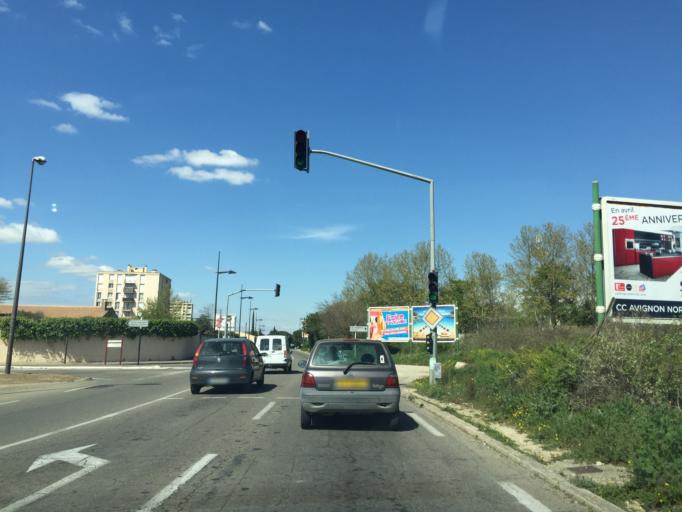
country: FR
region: Provence-Alpes-Cote d'Azur
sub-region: Departement du Vaucluse
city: Le Pontet
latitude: 43.9538
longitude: 4.8585
